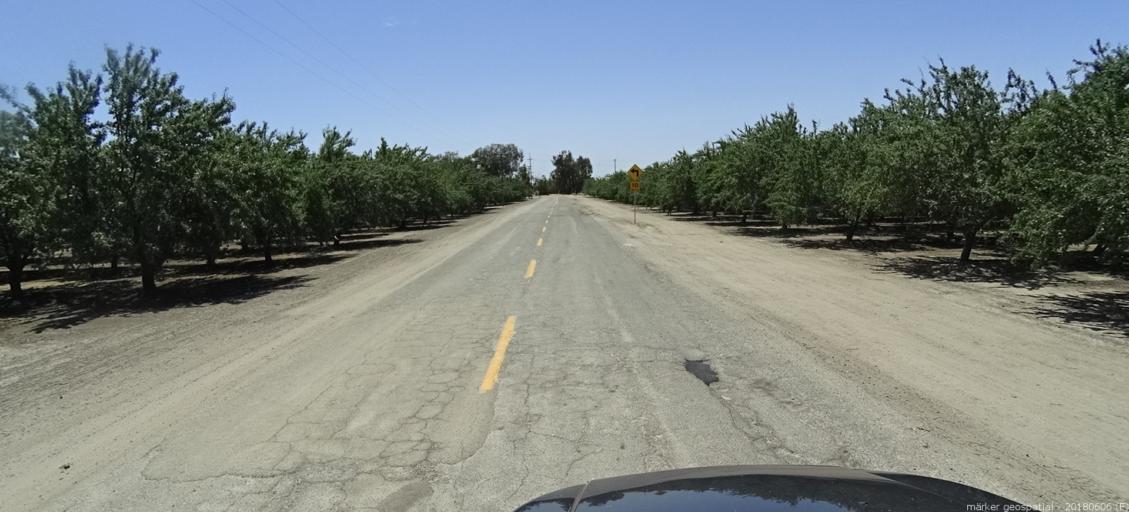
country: US
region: California
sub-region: Fresno County
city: Firebaugh
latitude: 36.8451
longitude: -120.4179
